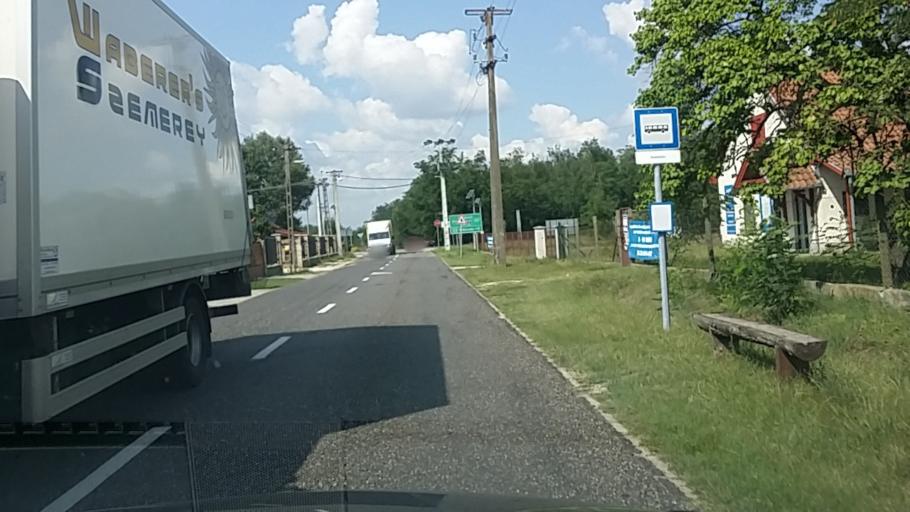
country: HU
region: Bacs-Kiskun
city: Lakitelek
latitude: 46.8674
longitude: 19.9609
